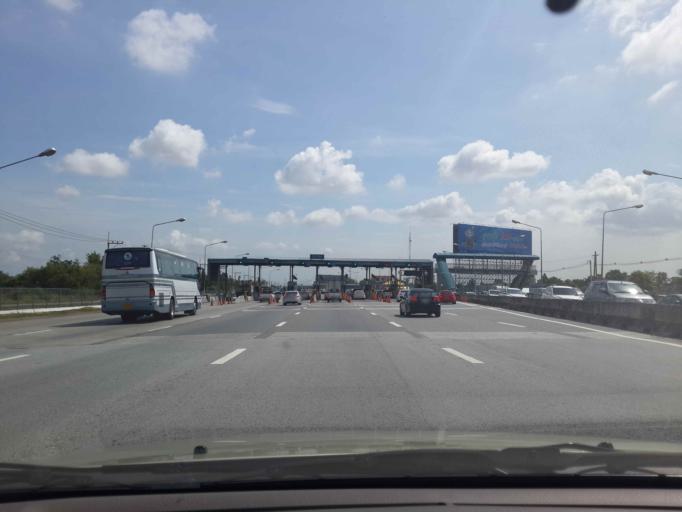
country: TH
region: Chon Buri
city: Chon Buri
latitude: 13.3863
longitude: 101.0457
